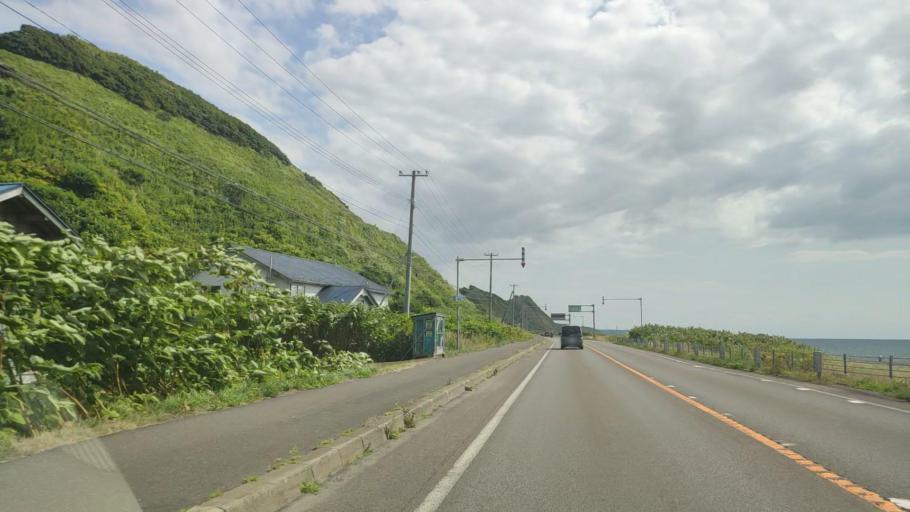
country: JP
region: Hokkaido
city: Rumoi
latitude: 44.2211
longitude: 141.6551
